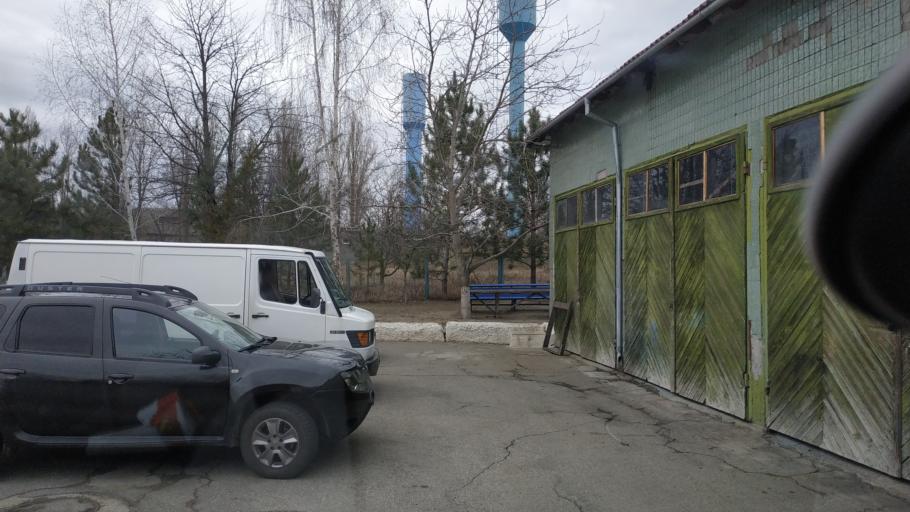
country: MD
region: Telenesti
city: Cocieri
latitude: 47.2932
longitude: 29.1188
